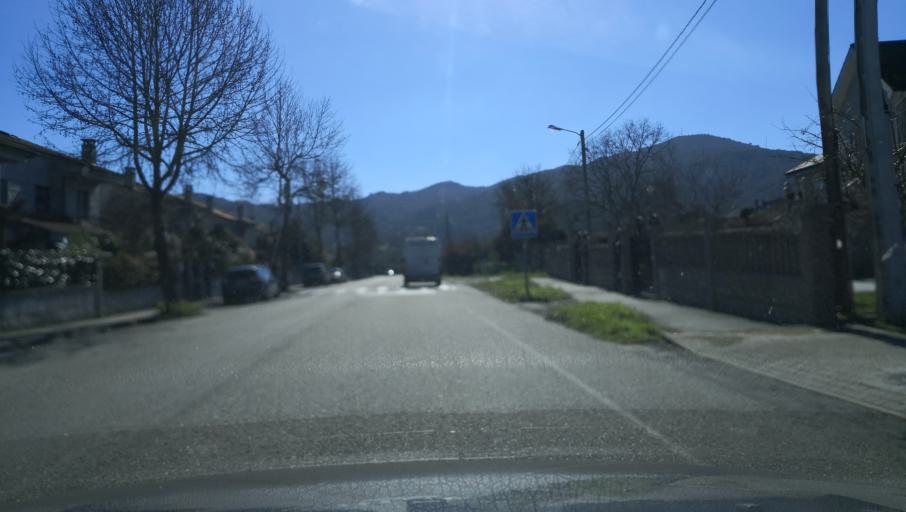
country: ES
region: Galicia
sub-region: Provincia de Ourense
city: Allariz
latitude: 42.1937
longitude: -7.8069
